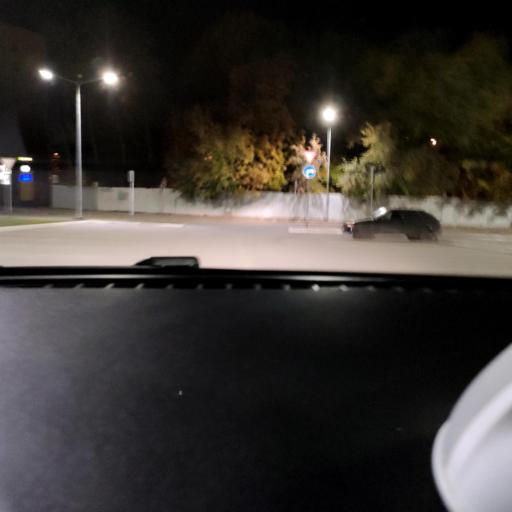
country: RU
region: Samara
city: Smyshlyayevka
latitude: 53.2207
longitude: 50.2758
